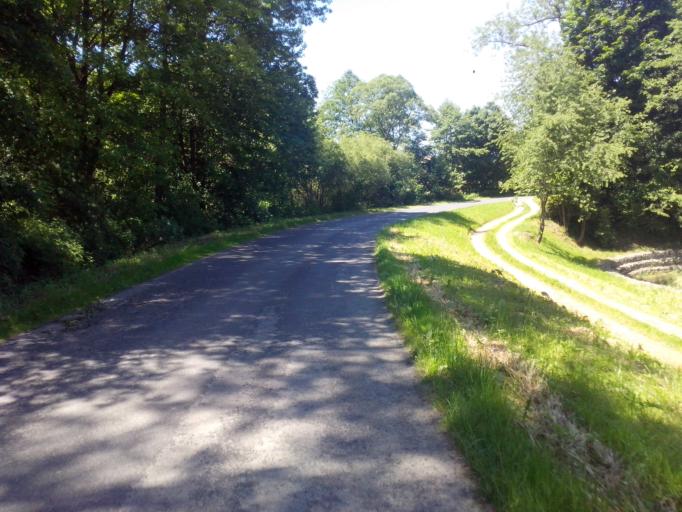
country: PL
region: Subcarpathian Voivodeship
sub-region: Powiat krosnienski
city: Wojaszowka
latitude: 49.7974
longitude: 21.7036
